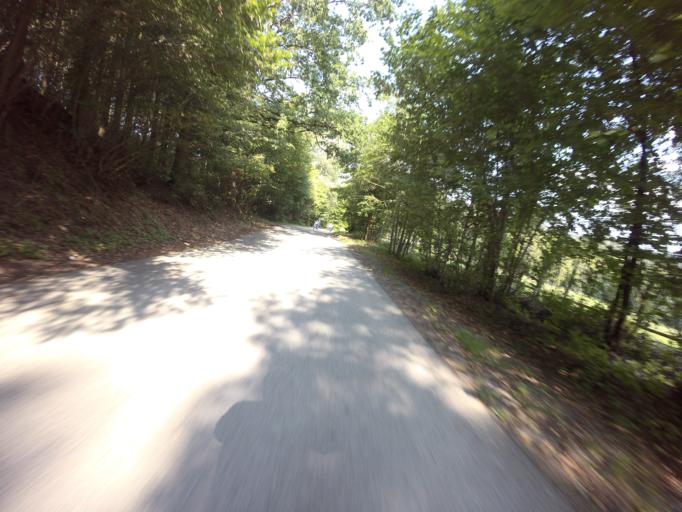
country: CZ
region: Jihocesky
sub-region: Okres Cesky Krumlov
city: Vyssi Brod
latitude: 48.6474
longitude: 14.3591
